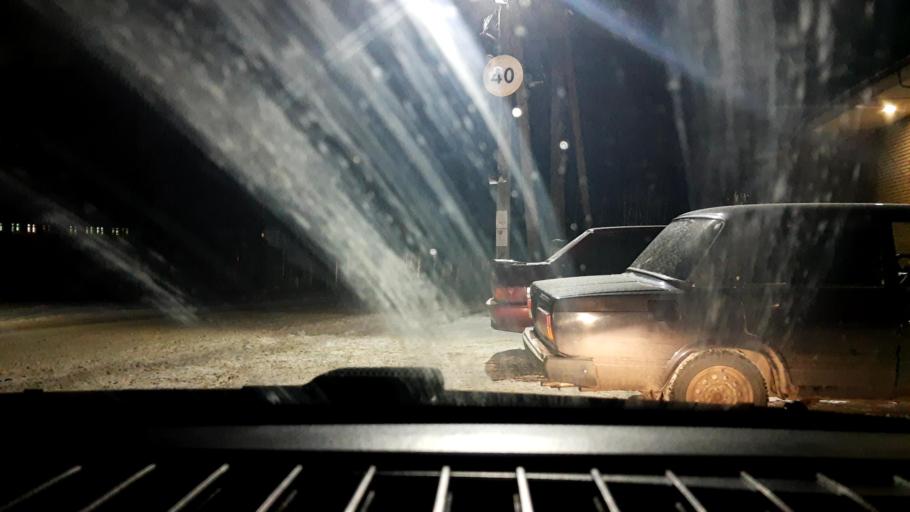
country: RU
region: Nizjnij Novgorod
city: Bogorodsk
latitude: 56.0967
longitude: 43.5334
